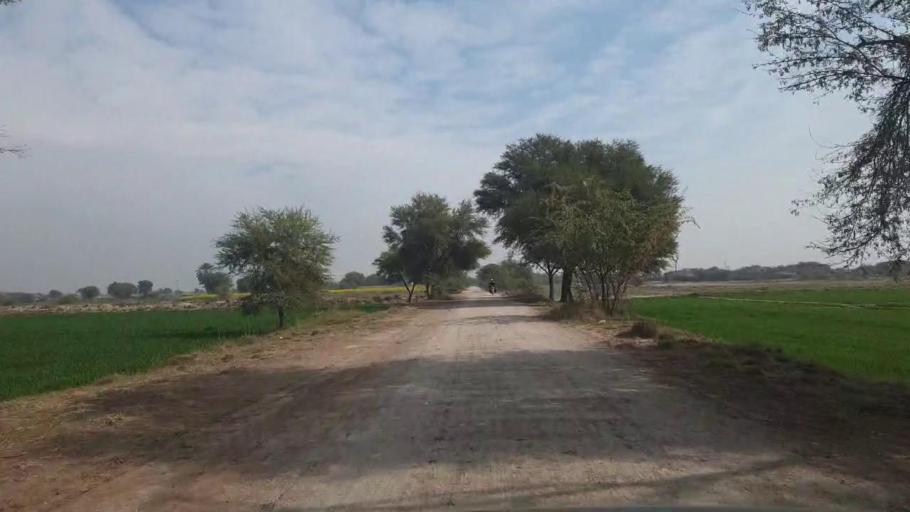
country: PK
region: Sindh
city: Nawabshah
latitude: 26.1138
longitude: 68.4912
